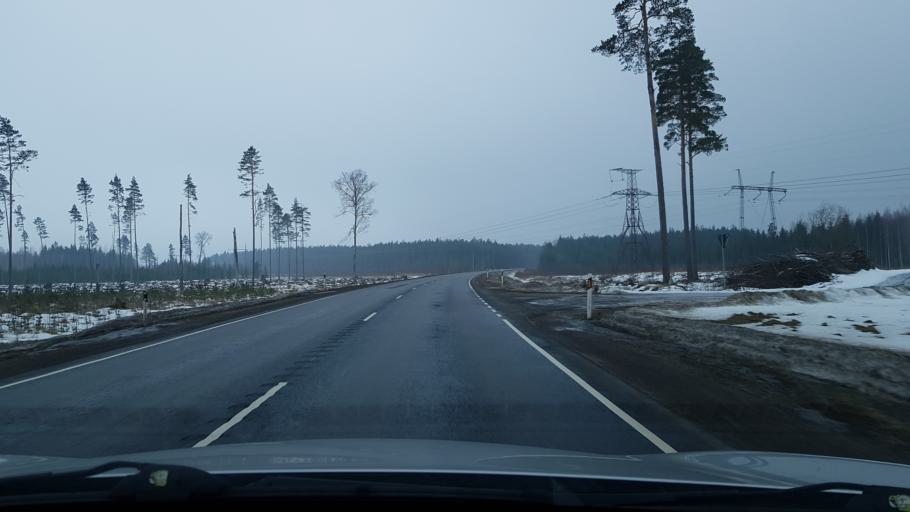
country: EE
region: Valgamaa
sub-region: Valga linn
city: Valga
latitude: 57.8816
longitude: 26.1630
